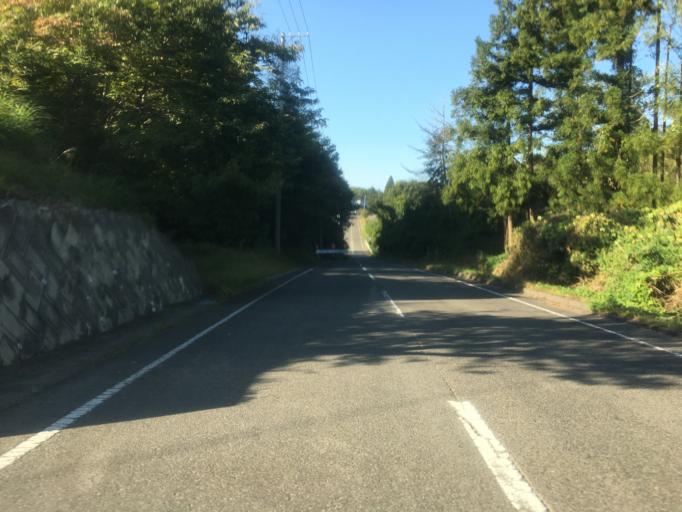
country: JP
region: Fukushima
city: Fukushima-shi
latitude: 37.6607
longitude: 140.4863
